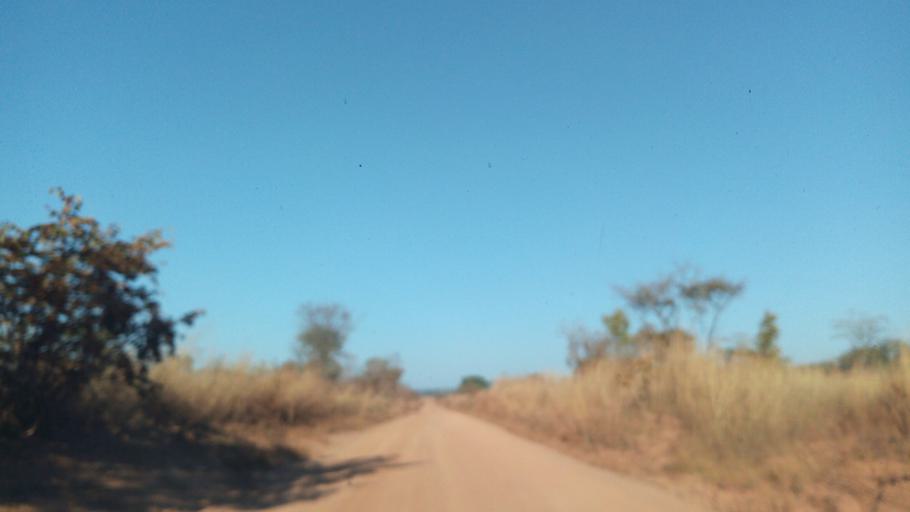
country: ZM
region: Luapula
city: Mwense
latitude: -10.5093
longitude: 28.4699
